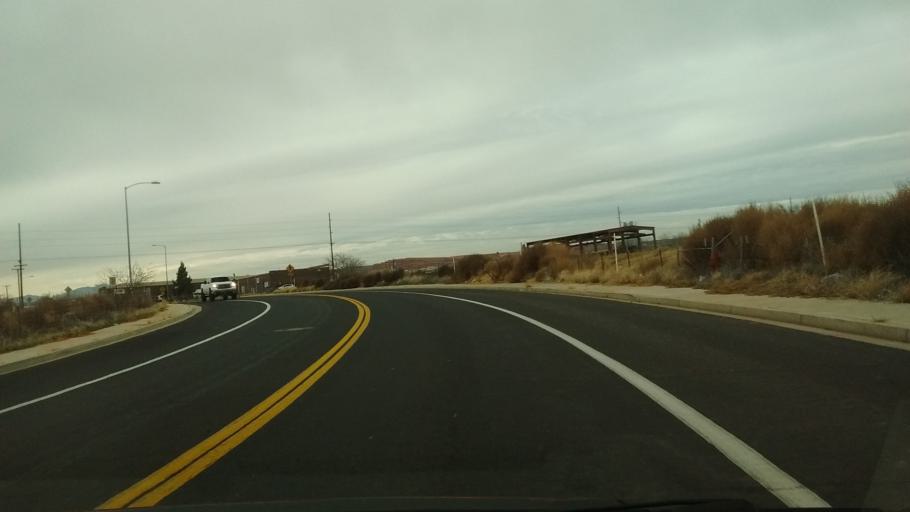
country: US
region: Utah
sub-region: Washington County
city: Washington
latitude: 37.1150
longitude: -113.5063
